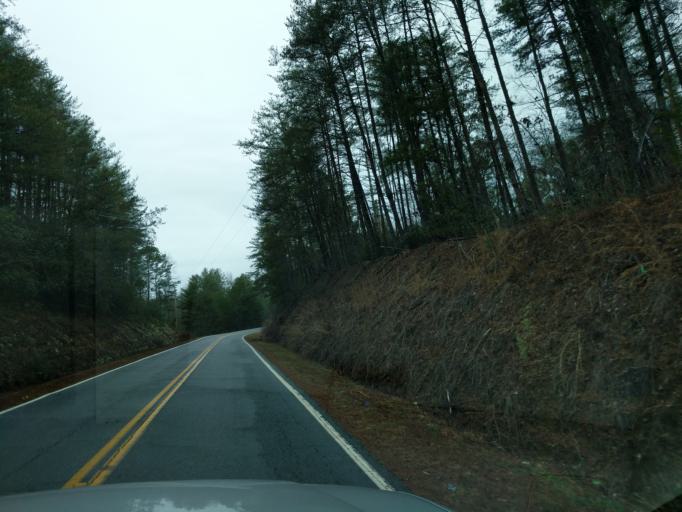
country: US
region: South Carolina
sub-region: Oconee County
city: Walhalla
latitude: 34.7875
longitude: -83.2149
